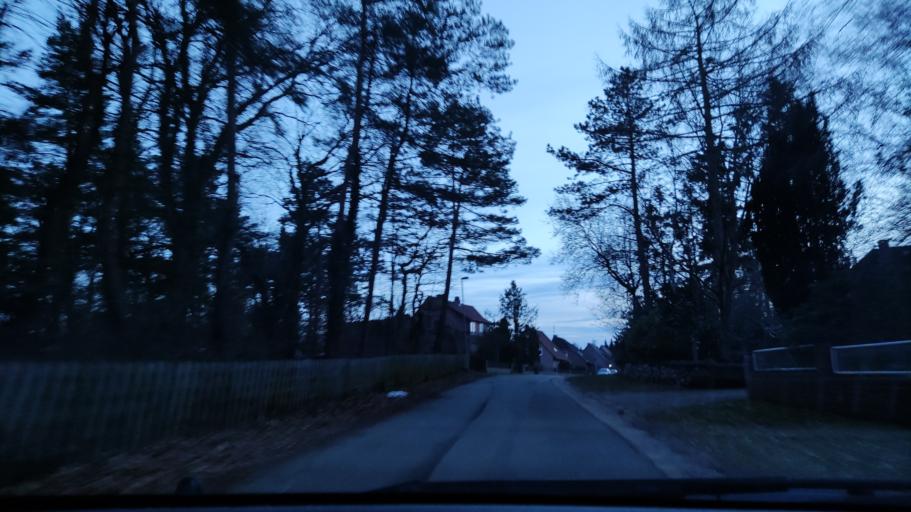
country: DE
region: Lower Saxony
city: Gohrde
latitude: 53.1611
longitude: 10.8650
